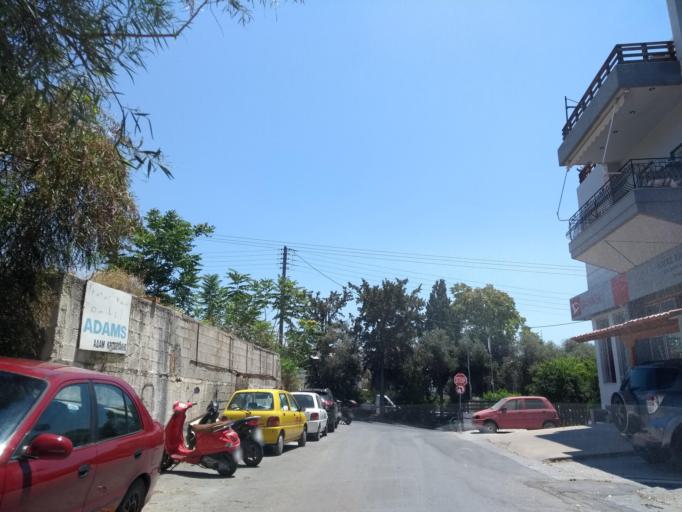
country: GR
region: Crete
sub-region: Nomos Irakleiou
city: Nea Alikarnassos
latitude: 35.3333
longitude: 25.1598
